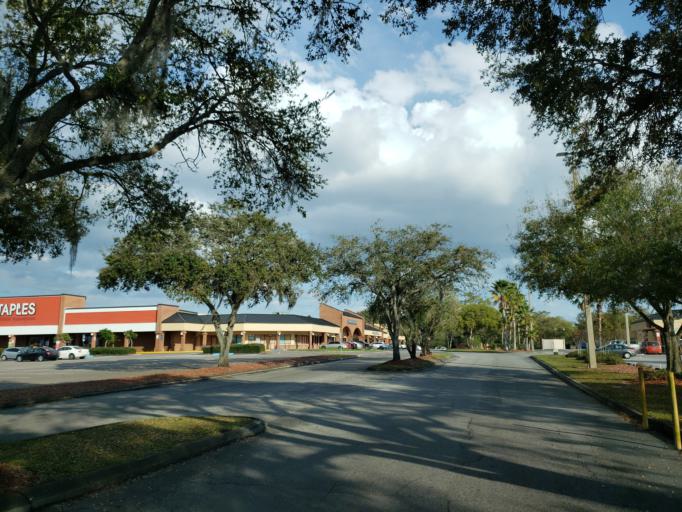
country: US
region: Florida
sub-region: Hillsborough County
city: Brandon
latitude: 27.9405
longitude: -82.3230
